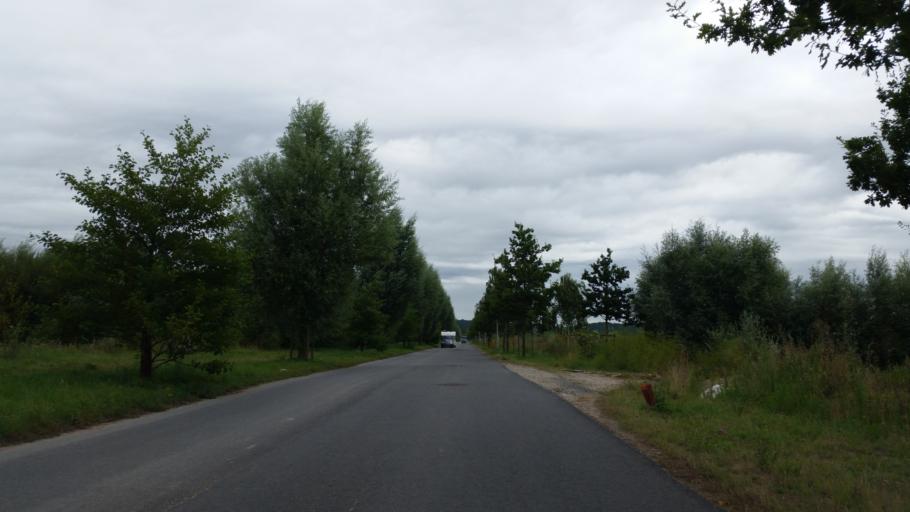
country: FR
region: Lower Normandy
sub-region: Departement du Calvados
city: La Riviere-Saint-Sauveur
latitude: 49.4199
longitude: 0.2629
